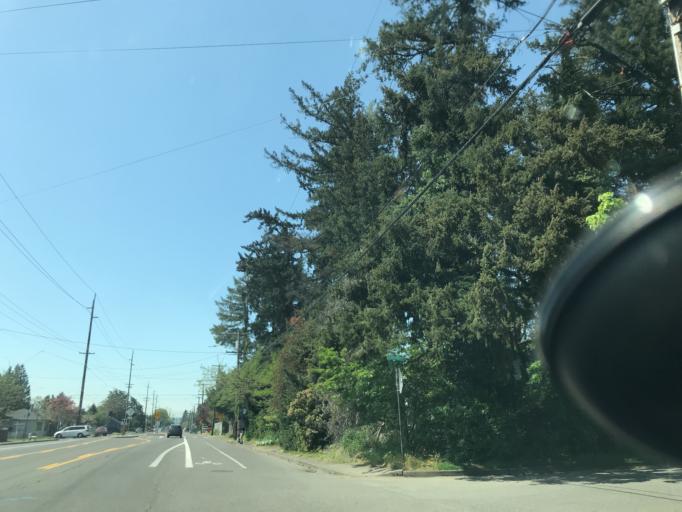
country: US
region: Oregon
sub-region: Multnomah County
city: Lents
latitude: 45.4899
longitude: -122.5597
